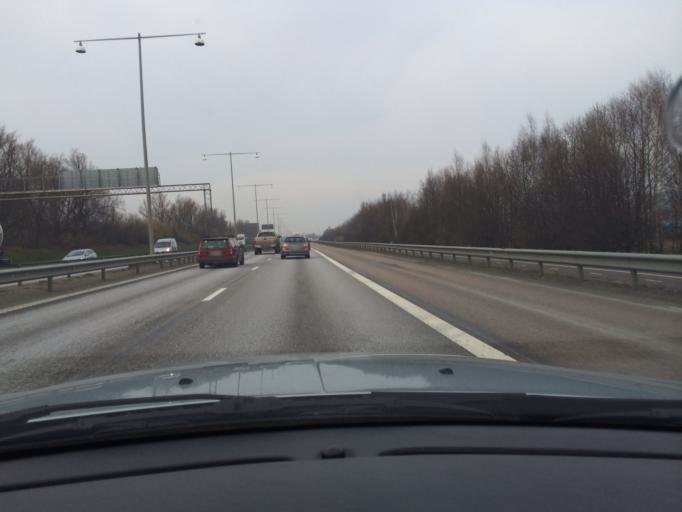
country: SE
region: Vaestra Goetaland
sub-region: Goteborg
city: Goeteborg
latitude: 57.7393
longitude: 11.9874
